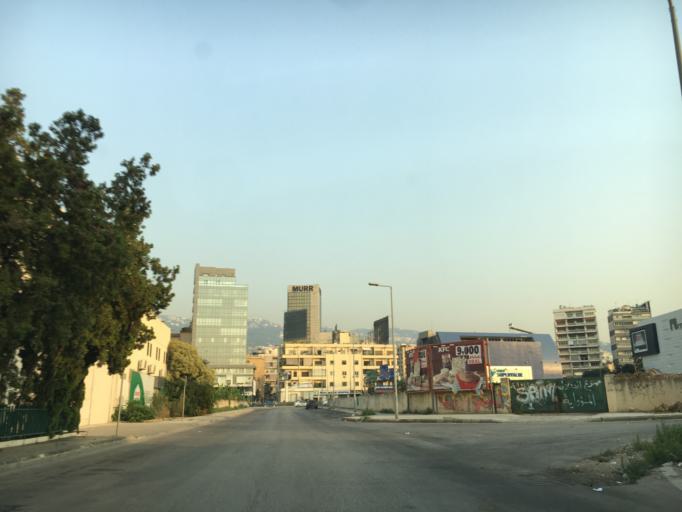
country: LB
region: Mont-Liban
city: Jdaidet el Matn
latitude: 33.9003
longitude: 35.5676
